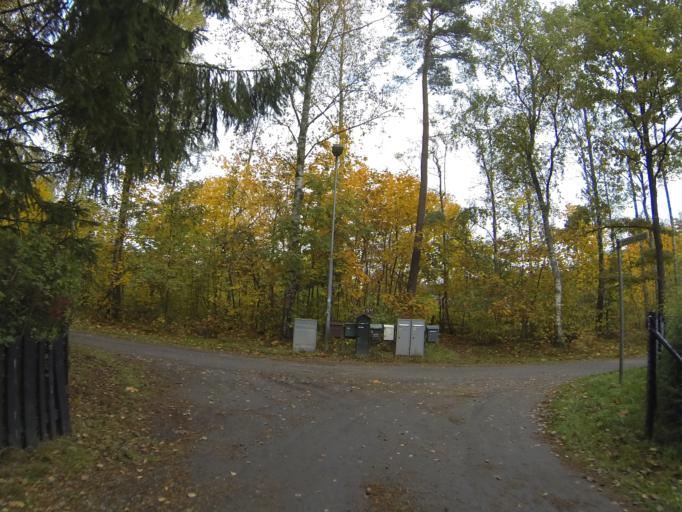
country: SE
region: Skane
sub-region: Sjobo Kommun
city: Sjoebo
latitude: 55.6337
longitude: 13.6652
